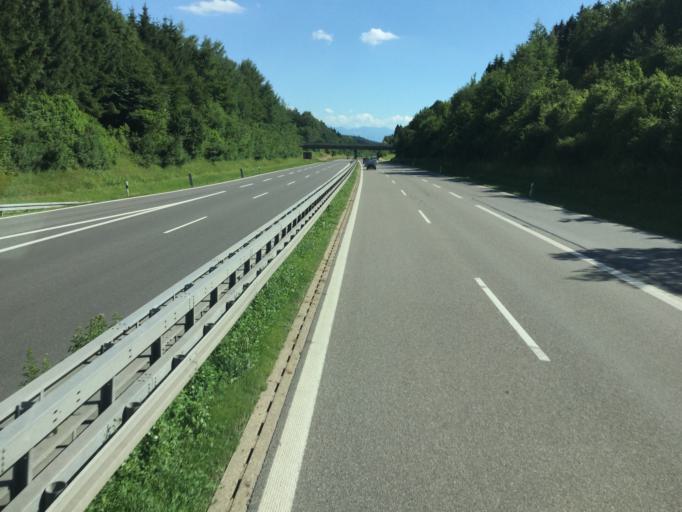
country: DE
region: Baden-Wuerttemberg
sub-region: Tuebingen Region
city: Amtzell
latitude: 47.6809
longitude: 9.7847
